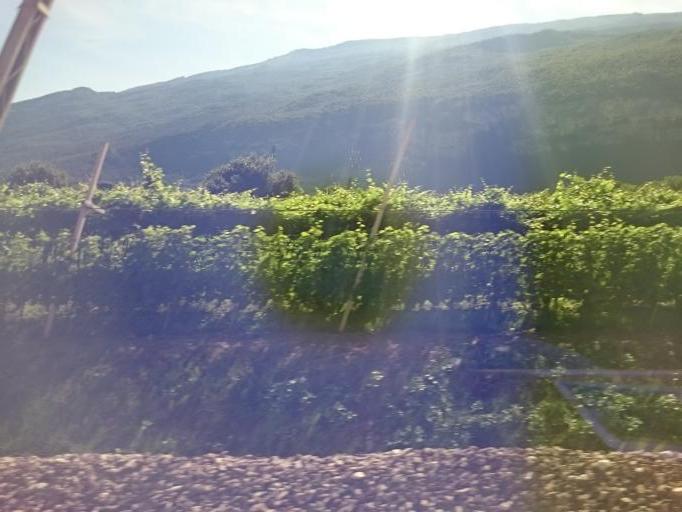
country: IT
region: Trentino-Alto Adige
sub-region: Provincia di Trento
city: Marco
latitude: 45.8296
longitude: 11.0033
